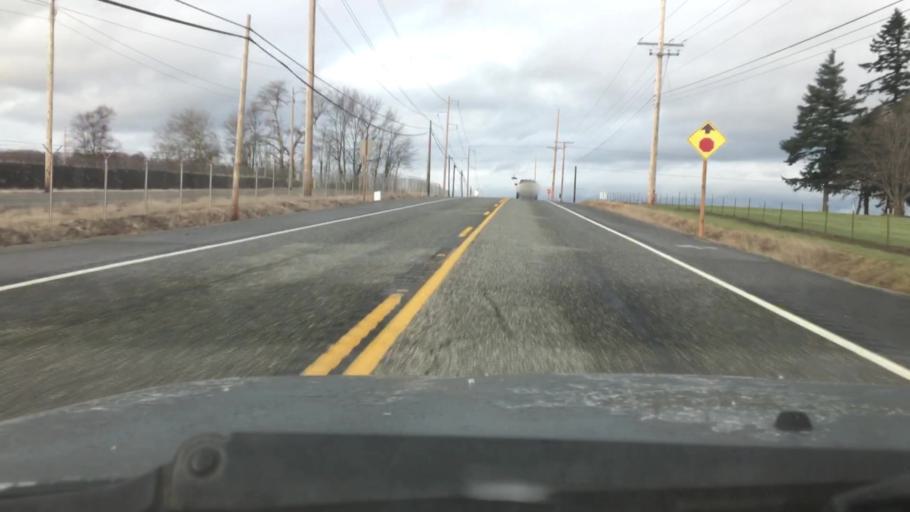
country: US
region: Washington
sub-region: Whatcom County
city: Ferndale
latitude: 48.8325
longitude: -122.6824
